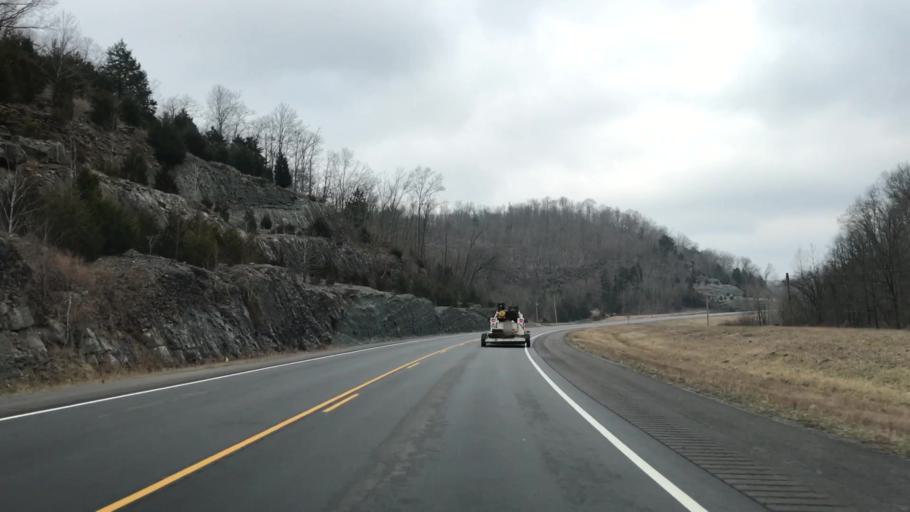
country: US
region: Kentucky
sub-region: Cumberland County
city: Burkesville
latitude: 36.9010
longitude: -85.4307
